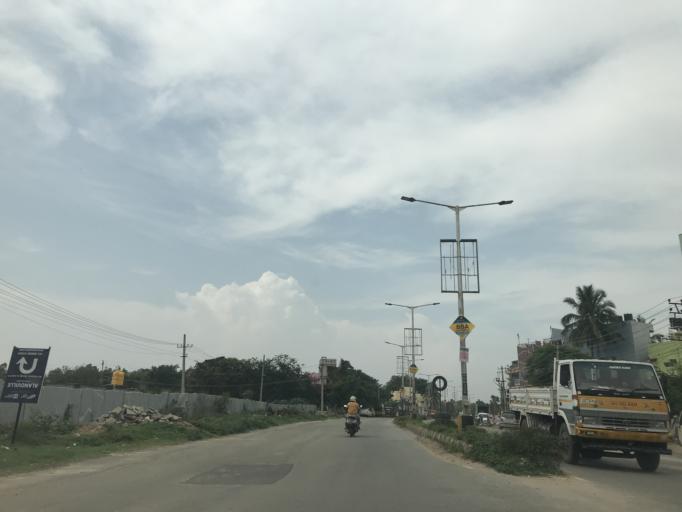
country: IN
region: Karnataka
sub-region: Bangalore Urban
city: Yelahanka
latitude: 13.0766
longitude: 77.6522
